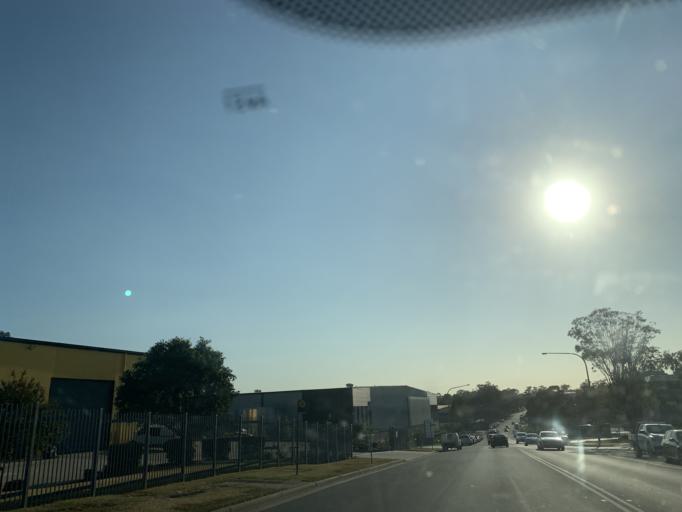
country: AU
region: New South Wales
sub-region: Blacktown
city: Doonside
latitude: -33.7976
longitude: 150.8802
